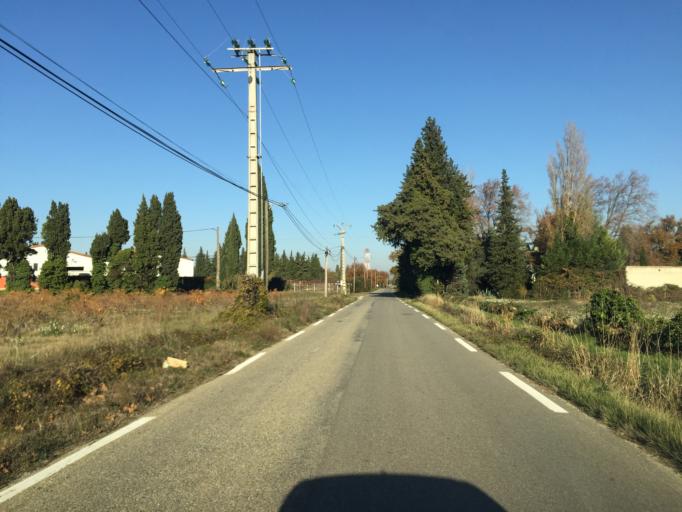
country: FR
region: Provence-Alpes-Cote d'Azur
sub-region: Departement du Vaucluse
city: Camaret-sur-Aigues
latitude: 44.1737
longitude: 4.8798
